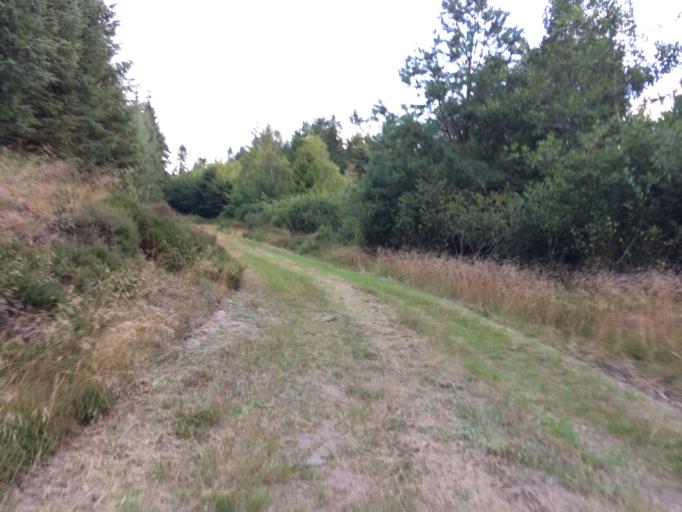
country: DK
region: Central Jutland
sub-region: Holstebro Kommune
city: Ulfborg
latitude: 56.2533
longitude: 8.3715
